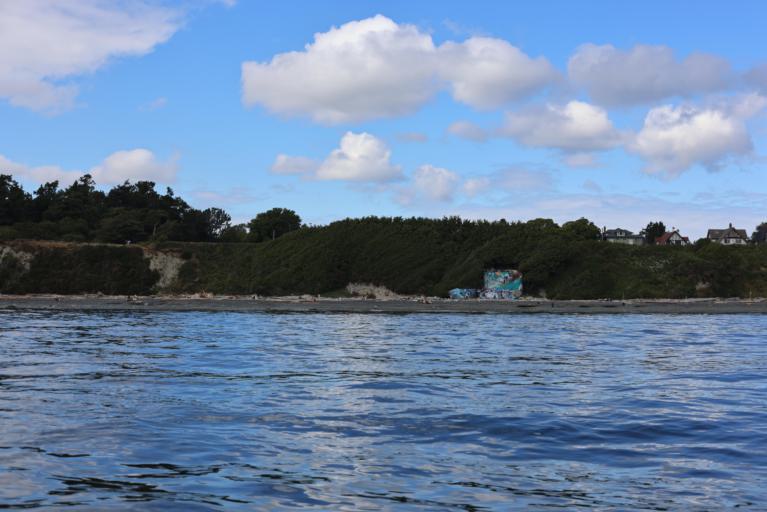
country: CA
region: British Columbia
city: Victoria
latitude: 48.4052
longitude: -123.3578
